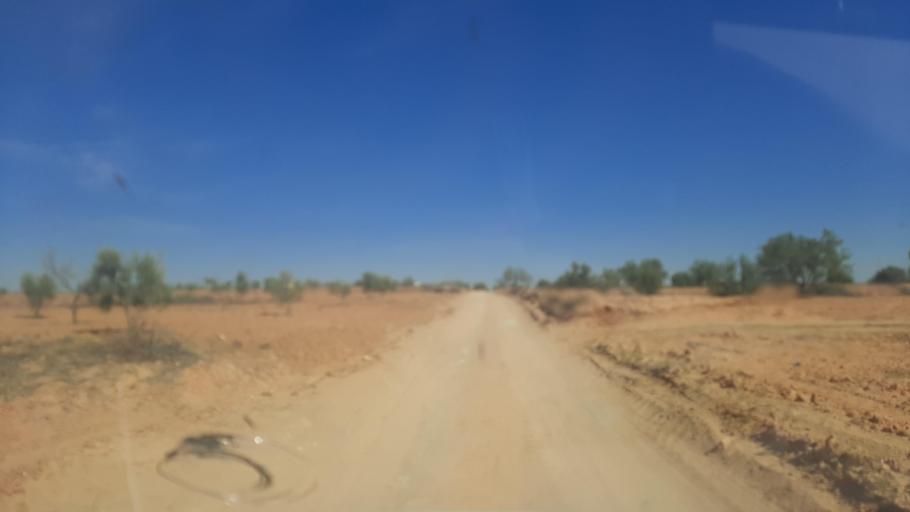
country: TN
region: Safaqis
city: Sfax
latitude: 34.8743
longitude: 10.5659
